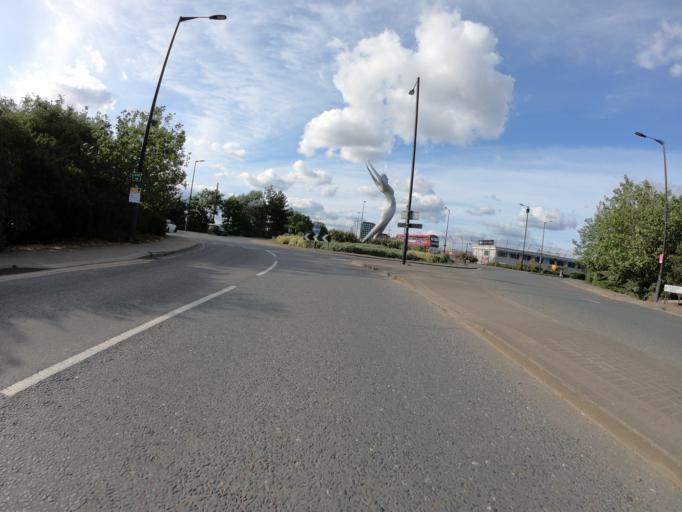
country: GB
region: England
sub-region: Greater London
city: Woolwich
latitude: 51.5043
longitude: 0.0395
